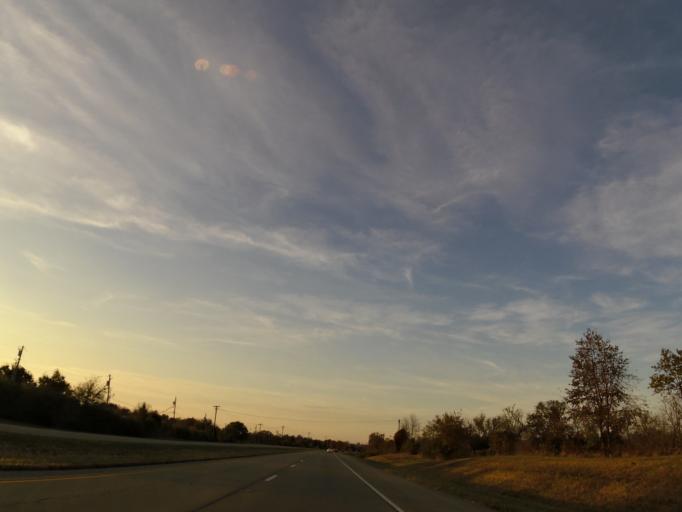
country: US
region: Kentucky
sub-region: Jessamine County
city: Nicholasville
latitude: 37.8600
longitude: -84.5916
